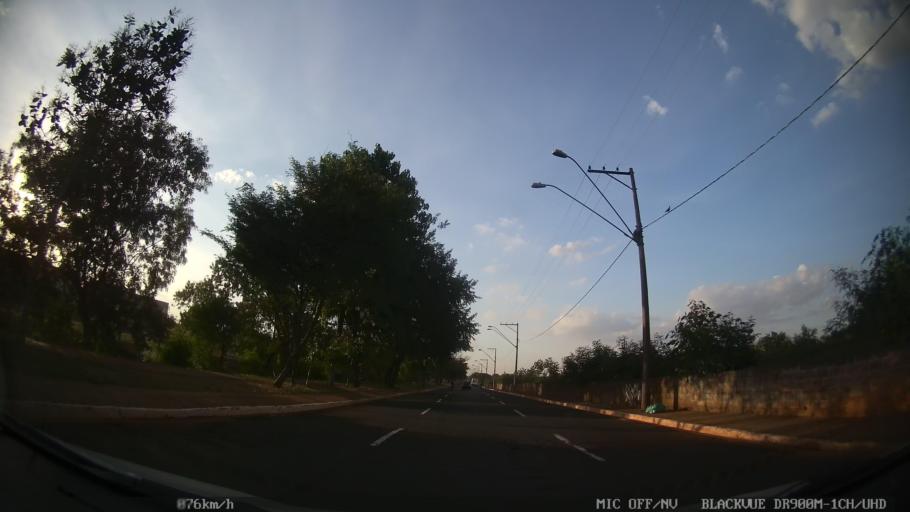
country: BR
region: Sao Paulo
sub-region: Ribeirao Preto
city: Ribeirao Preto
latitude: -21.1345
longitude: -47.8034
